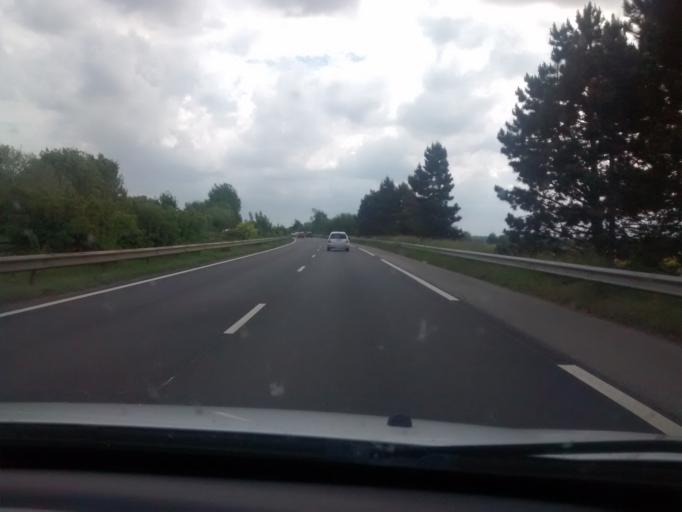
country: FR
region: Ile-de-France
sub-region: Departement des Yvelines
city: Le Perray-en-Yvelines
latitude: 48.7015
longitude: 1.8489
